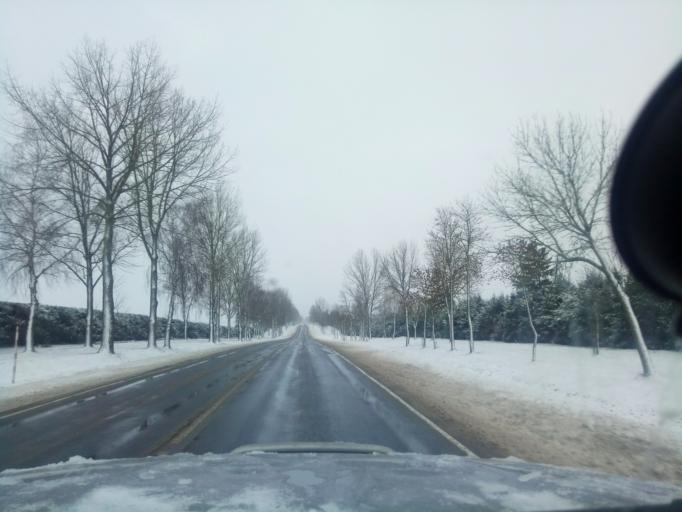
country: BY
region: Minsk
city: Haradzyeya
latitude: 53.3539
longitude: 26.5162
